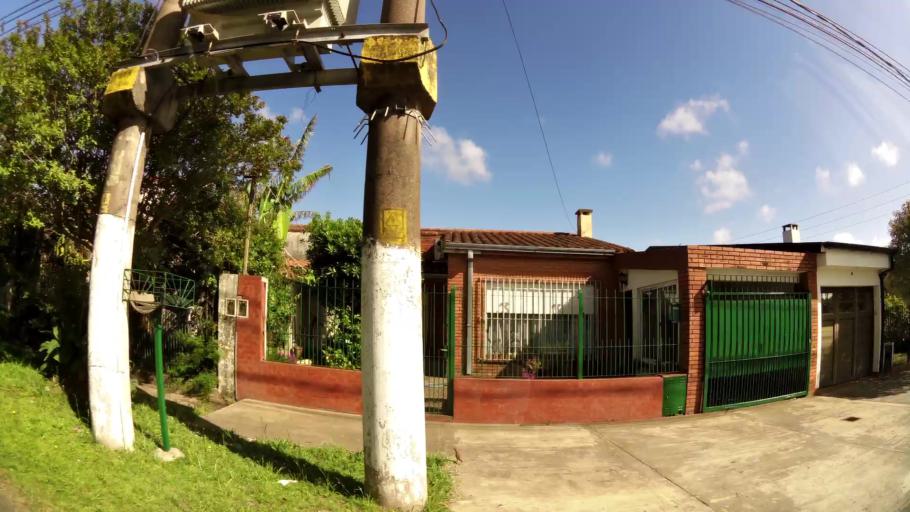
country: AR
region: Buenos Aires
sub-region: Partido de Quilmes
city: Quilmes
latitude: -34.7875
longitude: -58.1517
